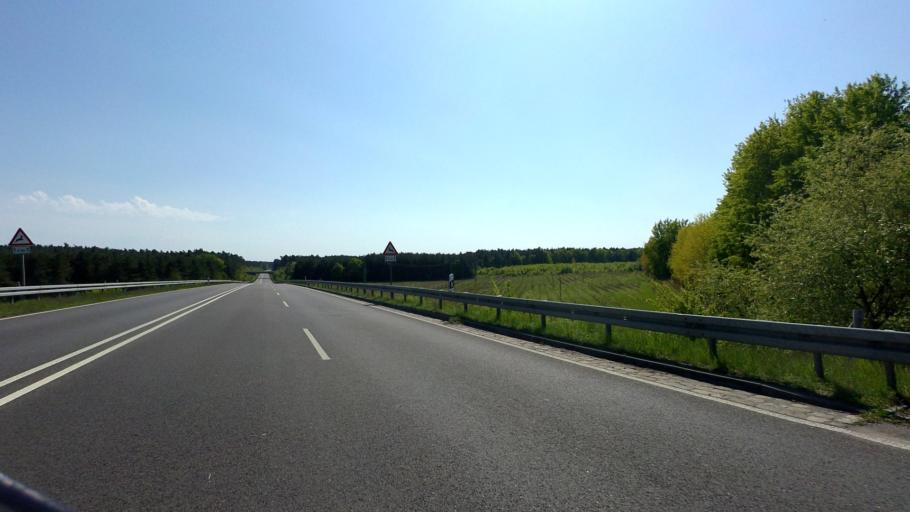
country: DE
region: Brandenburg
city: Beeskow
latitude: 52.1655
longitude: 14.2167
